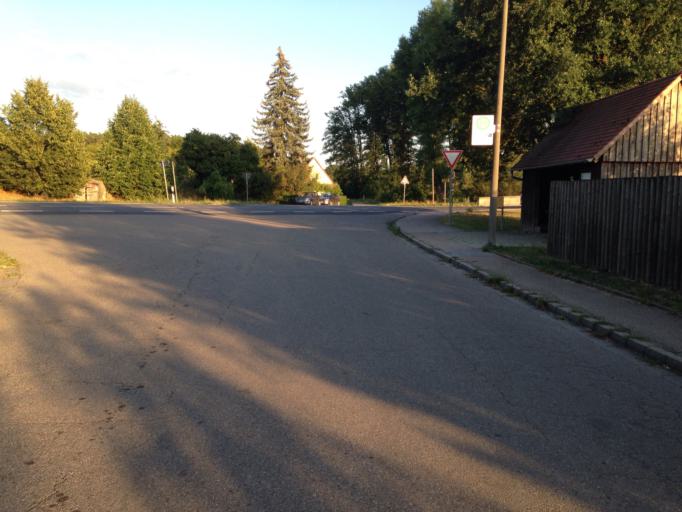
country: DE
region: Bavaria
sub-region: Regierungsbezirk Mittelfranken
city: Hilpoltstein
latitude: 49.1586
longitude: 11.1730
